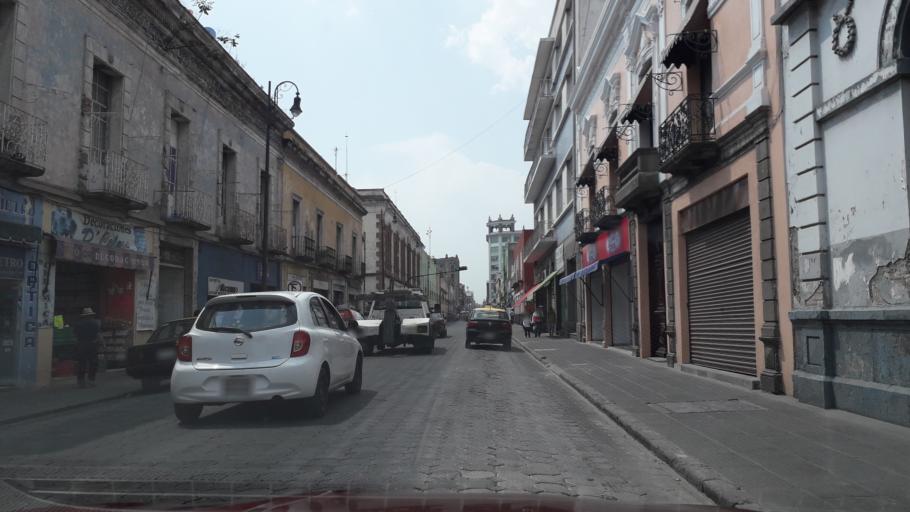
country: MX
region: Puebla
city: Puebla
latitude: 19.0473
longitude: -98.2022
